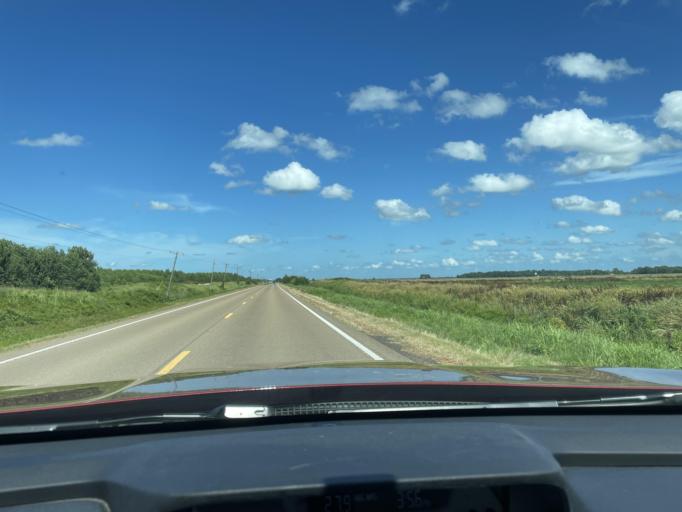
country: US
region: Mississippi
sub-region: Humphreys County
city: Belzoni
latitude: 33.1828
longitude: -90.6194
